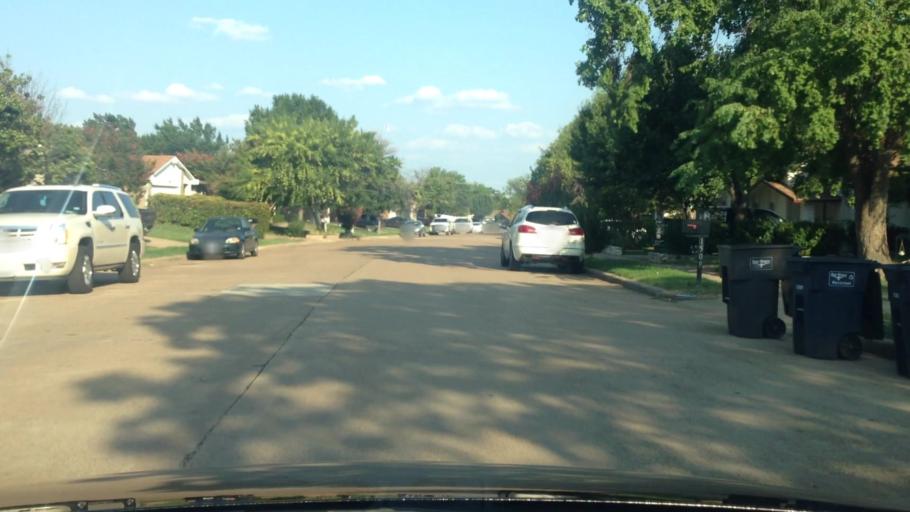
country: US
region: Texas
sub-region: Tarrant County
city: Edgecliff Village
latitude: 32.6449
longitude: -97.3425
